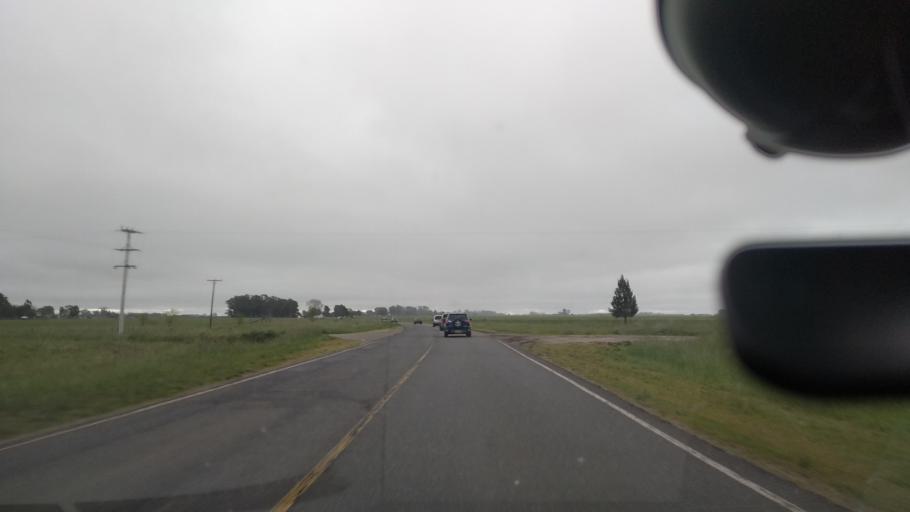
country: AR
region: Buenos Aires
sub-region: Partido de Magdalena
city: Magdalena
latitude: -35.2205
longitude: -57.7372
